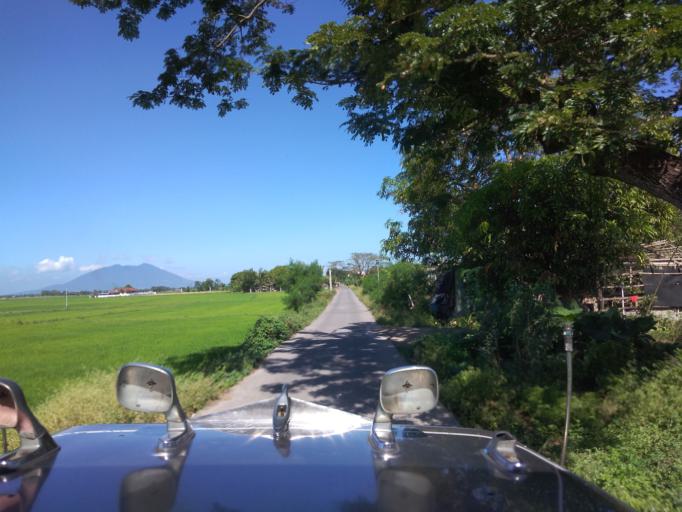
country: PH
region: Central Luzon
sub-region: Province of Pampanga
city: Batasan Bata
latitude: 15.1508
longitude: 120.9257
